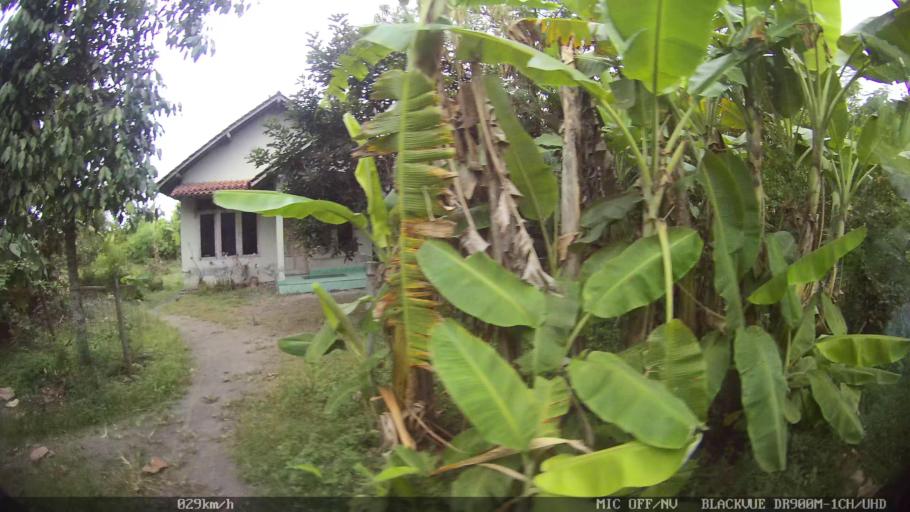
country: ID
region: Daerah Istimewa Yogyakarta
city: Sewon
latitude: -7.8598
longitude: 110.4003
